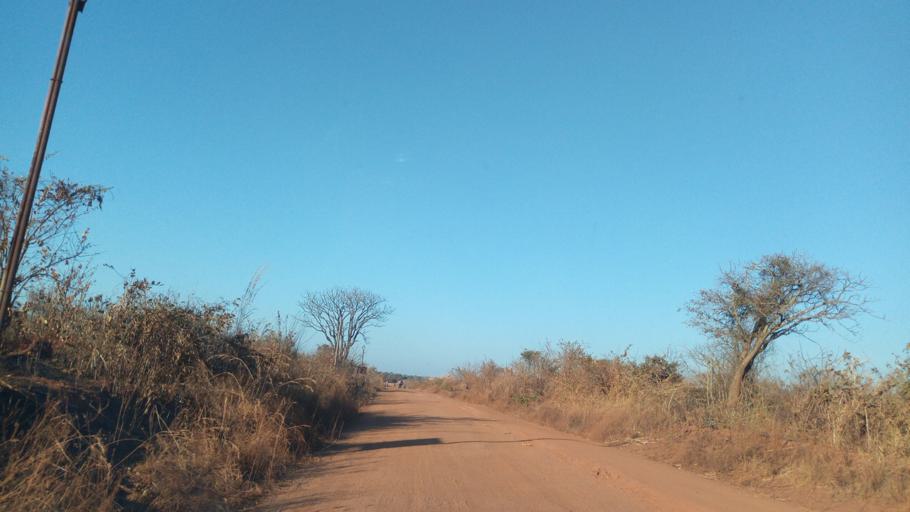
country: ZM
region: Luapula
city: Mwense
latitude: -10.4127
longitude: 28.6093
